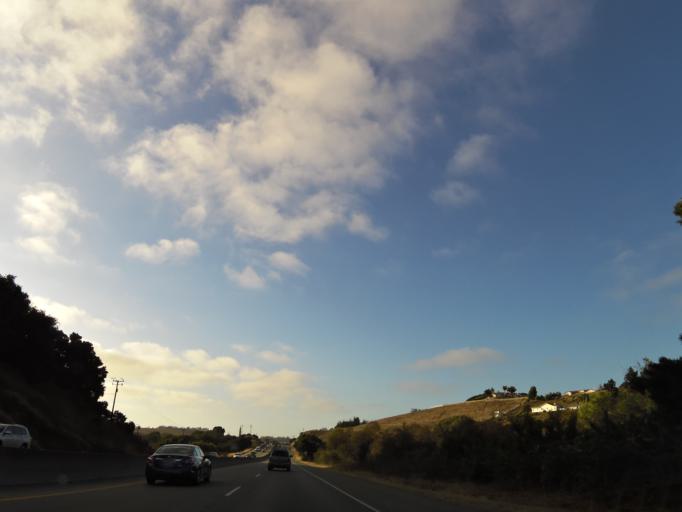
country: US
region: California
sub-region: Monterey County
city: Prunedale
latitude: 36.7597
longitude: -121.6661
